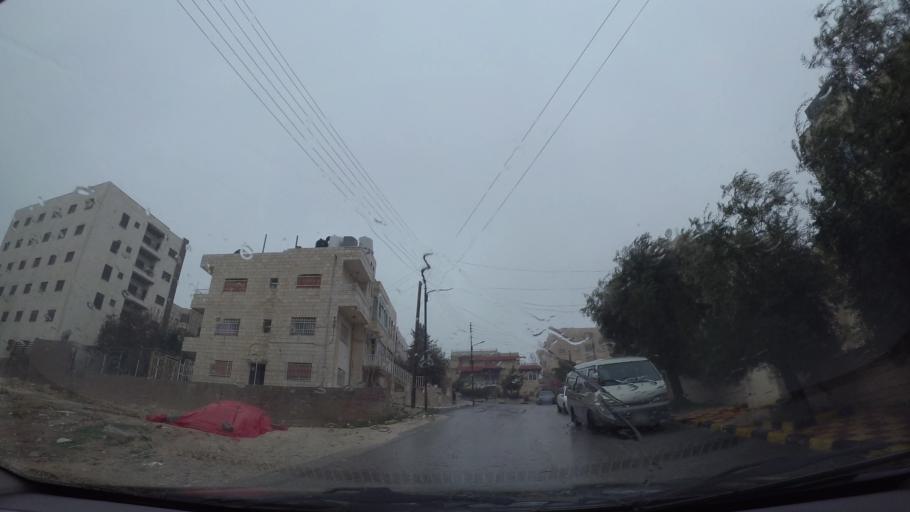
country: JO
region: Amman
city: Al Jubayhah
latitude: 32.0110
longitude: 35.8840
